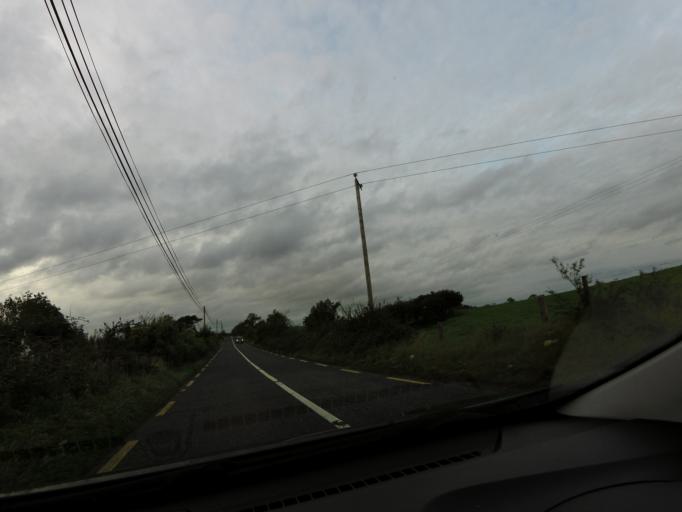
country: IE
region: Leinster
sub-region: An Iarmhi
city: Athlone
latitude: 53.3790
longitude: -7.8620
